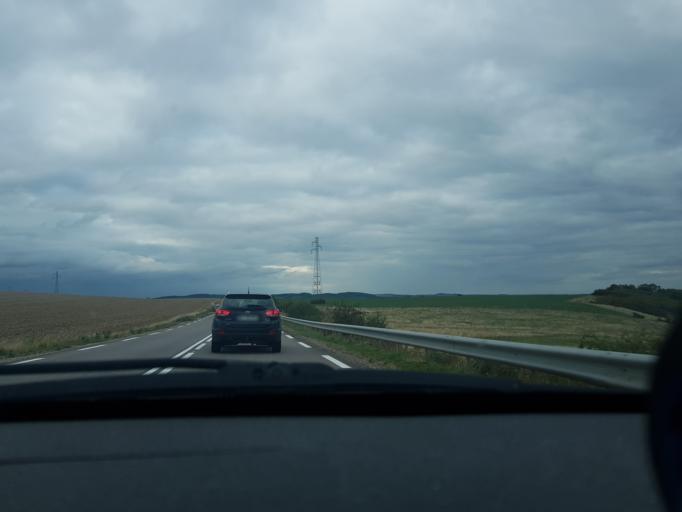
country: FR
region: Lorraine
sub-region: Departement de la Moselle
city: Morhange
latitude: 48.9261
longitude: 6.5977
